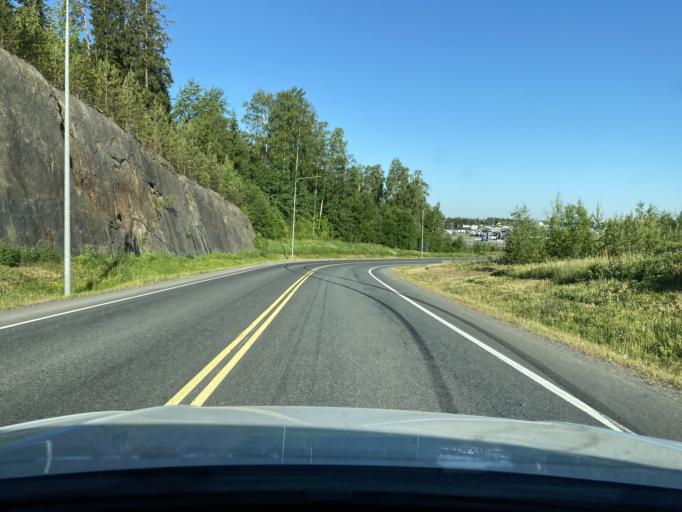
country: FI
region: Haeme
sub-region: Forssa
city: Forssa
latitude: 60.8244
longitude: 23.5829
